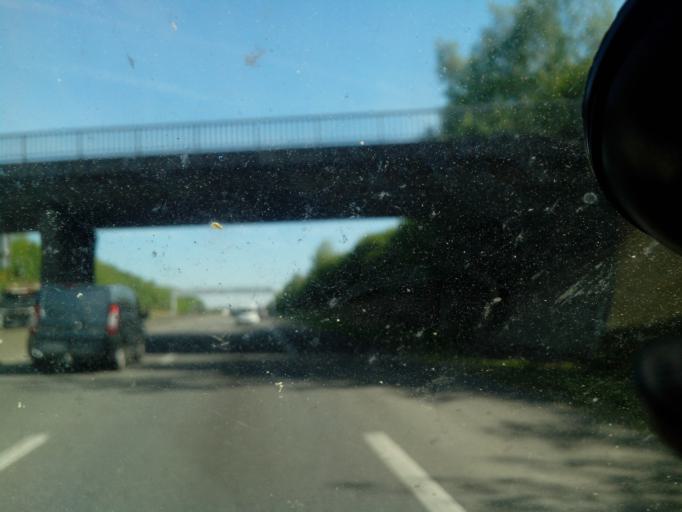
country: FR
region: Pays de la Loire
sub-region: Departement de la Loire-Atlantique
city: Orvault
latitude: 47.2447
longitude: -1.6220
